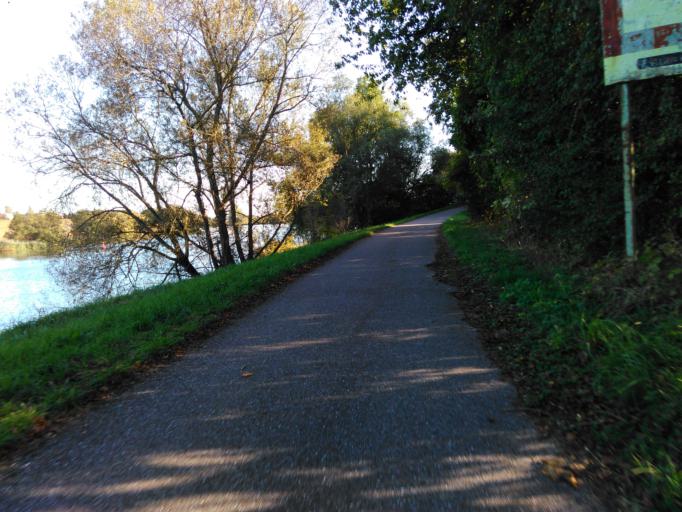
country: FR
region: Lorraine
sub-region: Departement de la Moselle
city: Bousse
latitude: 49.2887
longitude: 6.1815
